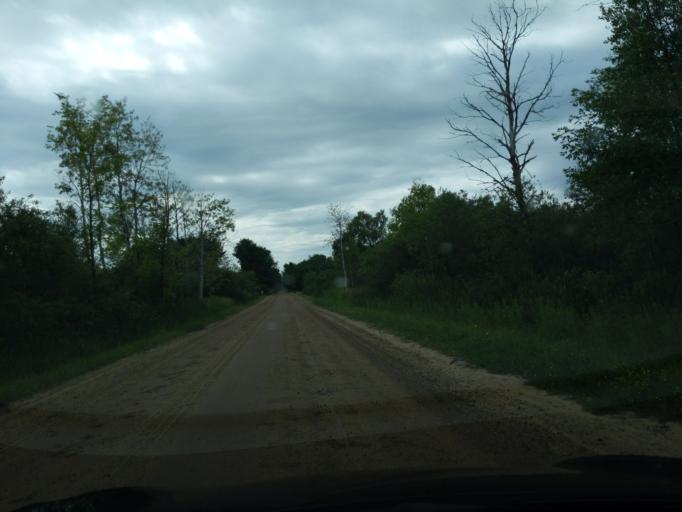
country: US
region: Michigan
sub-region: Clare County
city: Harrison
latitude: 44.0024
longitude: -84.9650
